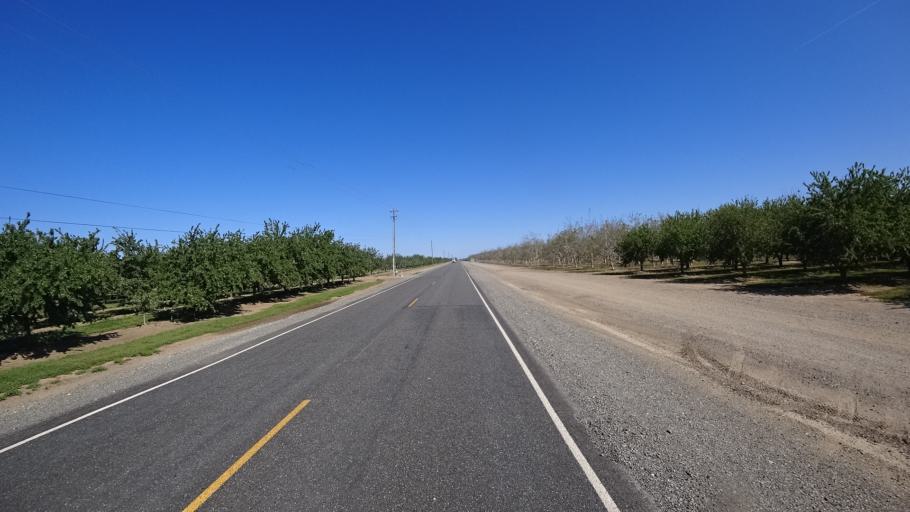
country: US
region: California
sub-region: Glenn County
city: Willows
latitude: 39.6319
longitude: -122.1040
